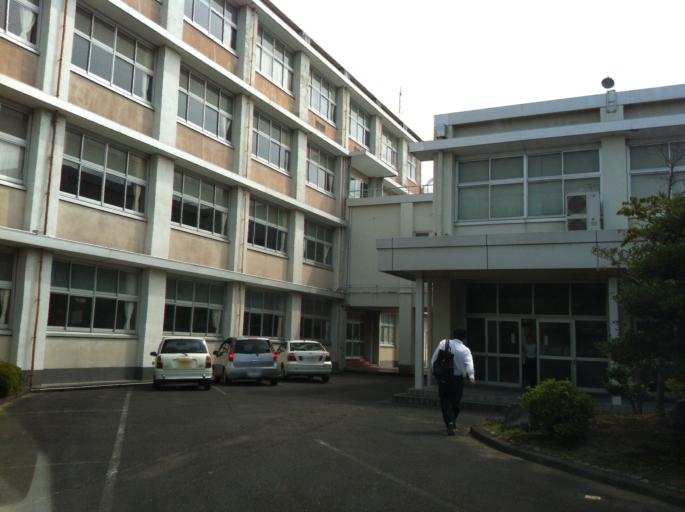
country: JP
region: Shizuoka
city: Shimada
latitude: 34.8348
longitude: 138.1830
